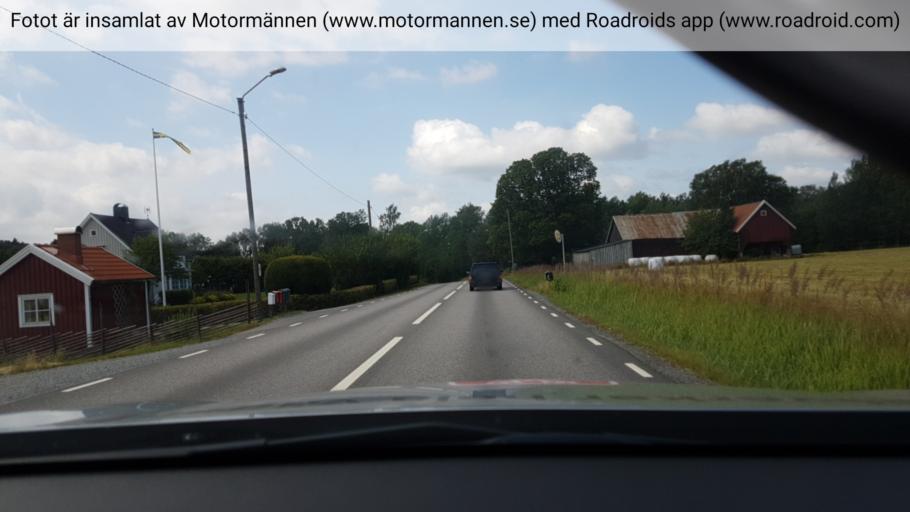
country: SE
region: Vaestra Goetaland
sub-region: Marks Kommun
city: Kinna
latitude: 57.4738
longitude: 12.7191
